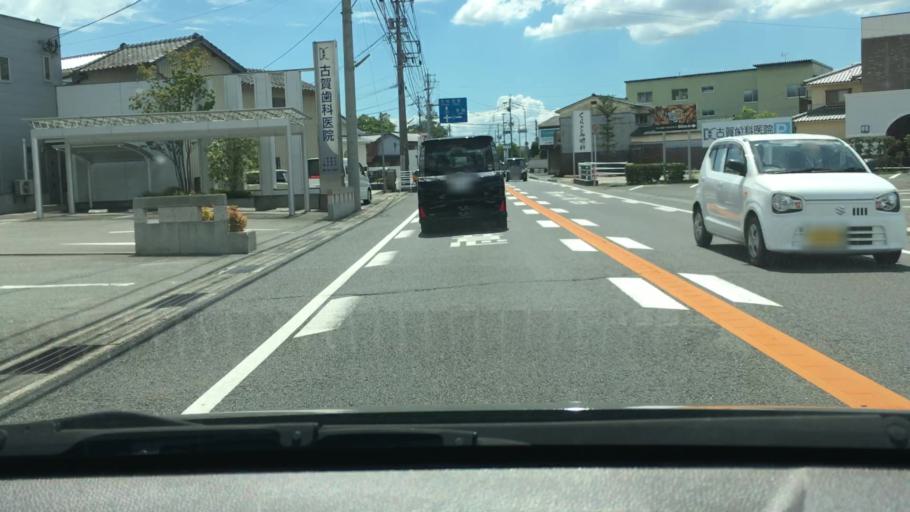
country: JP
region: Saga Prefecture
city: Kanzakimachi-kanzaki
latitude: 33.3127
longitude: 130.3745
